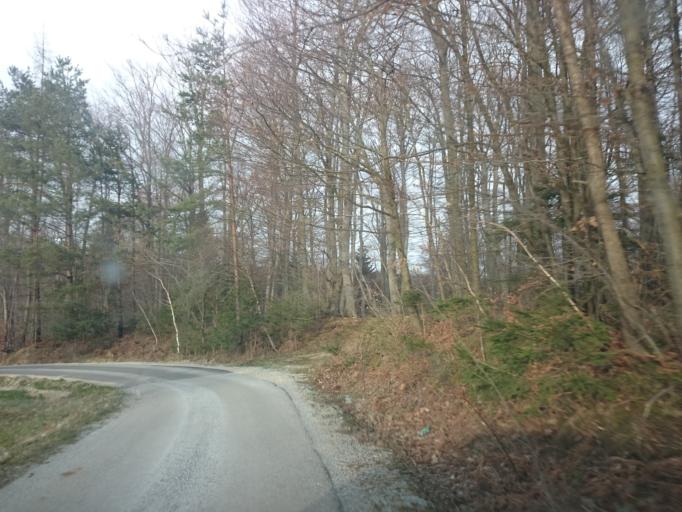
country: SI
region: Dobje
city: Dobje pri Planini
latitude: 46.1510
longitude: 15.3677
